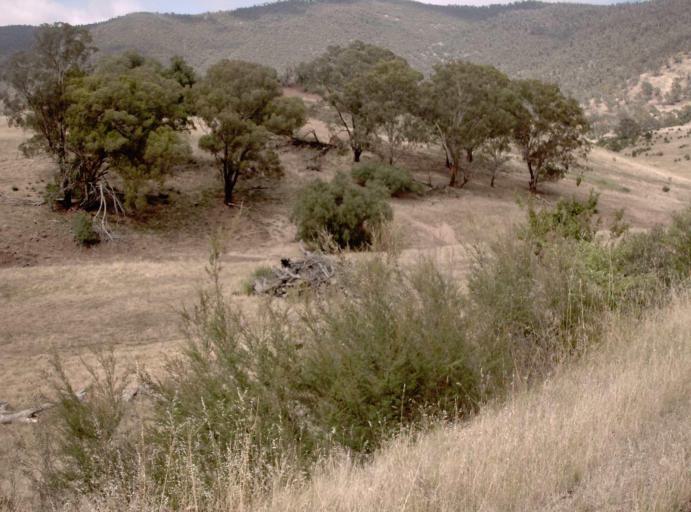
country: AU
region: Victoria
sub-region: Wellington
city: Heyfield
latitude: -37.6254
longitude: 146.6227
